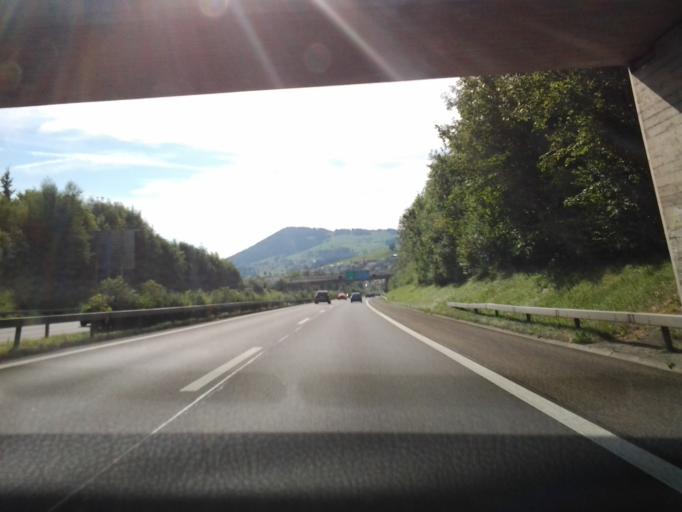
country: CH
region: Zurich
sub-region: Bezirk Horgen
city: Richterswil
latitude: 47.2004
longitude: 8.6944
